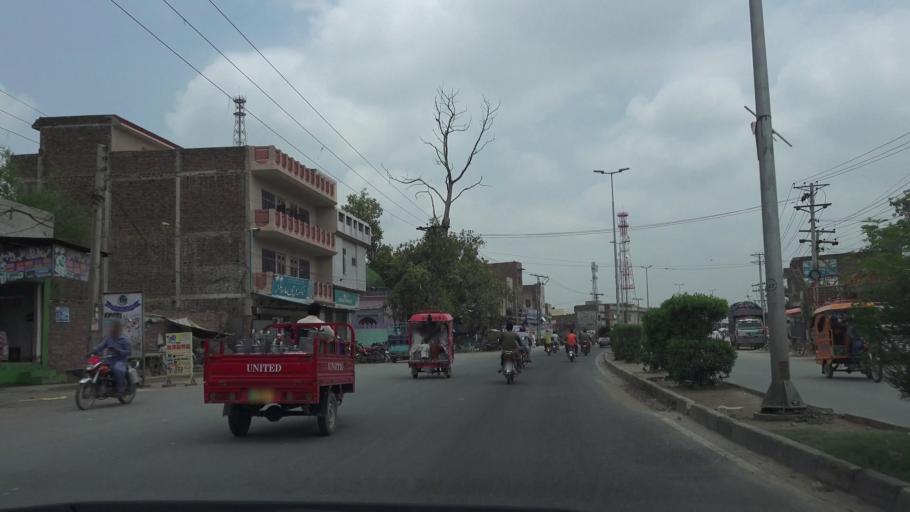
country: PK
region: Punjab
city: Faisalabad
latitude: 31.4006
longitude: 73.1456
